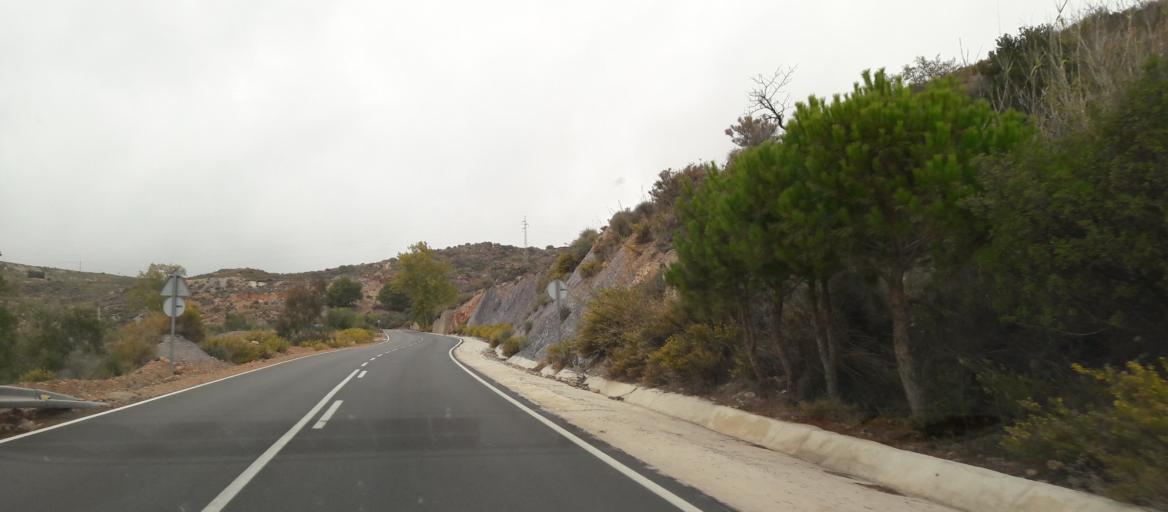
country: ES
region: Andalusia
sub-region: Provincia de Almeria
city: Enix
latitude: 36.8740
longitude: -2.6176
